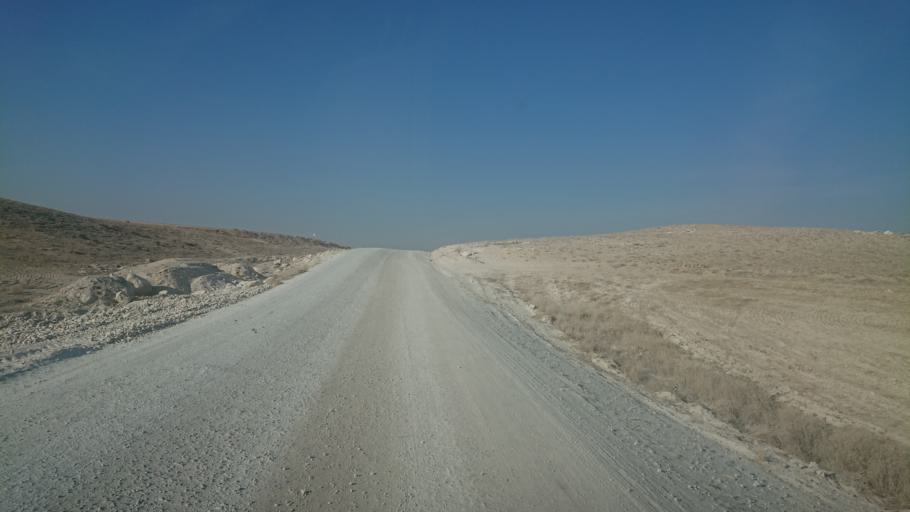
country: TR
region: Aksaray
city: Sultanhani
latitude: 38.0837
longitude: 33.6154
